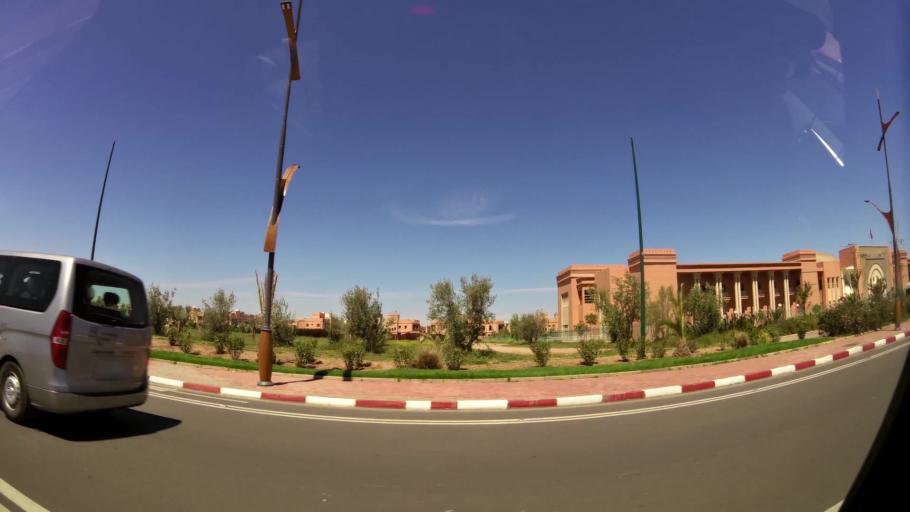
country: MA
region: Marrakech-Tensift-Al Haouz
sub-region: Marrakech
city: Marrakesh
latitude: 31.6101
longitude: -7.9951
